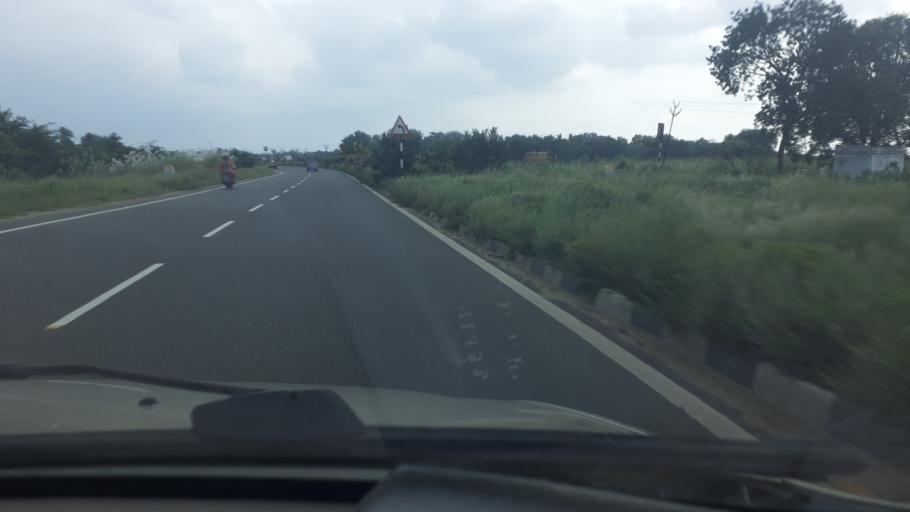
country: IN
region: Tamil Nadu
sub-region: Virudhunagar
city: Virudunagar
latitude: 9.6876
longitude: 77.9706
